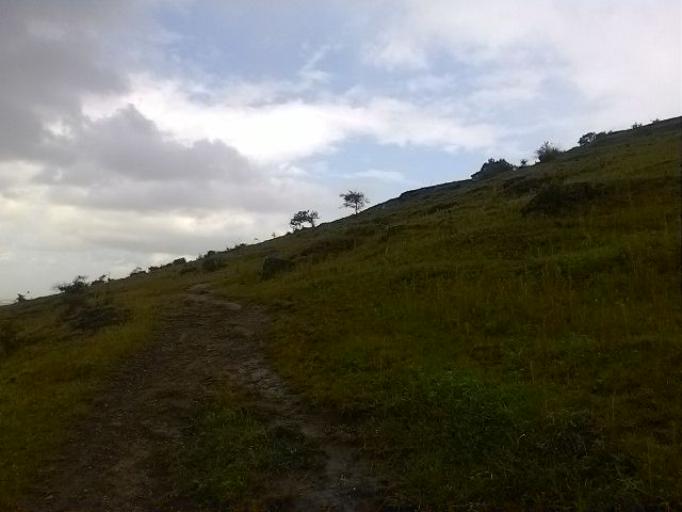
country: IN
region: Maharashtra
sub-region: Pune Division
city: Khadki
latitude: 18.5488
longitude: 73.7844
